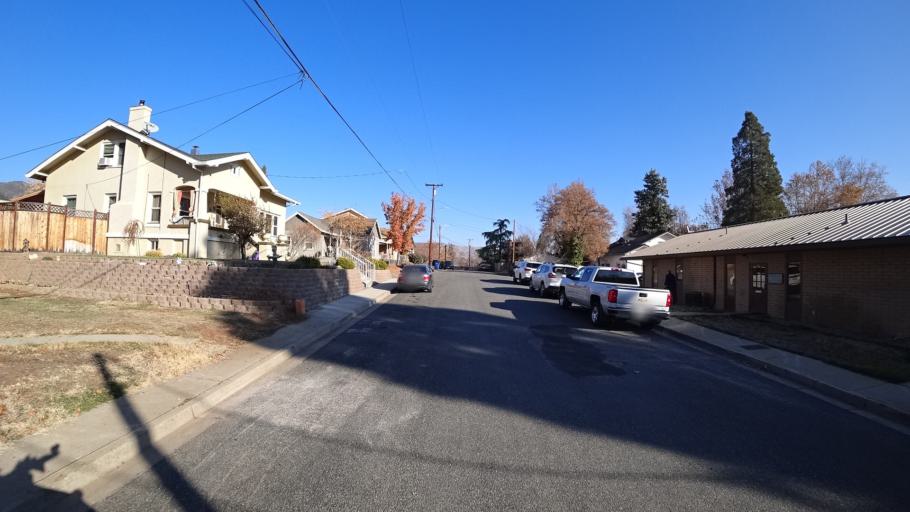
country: US
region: California
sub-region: Siskiyou County
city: Yreka
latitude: 41.7375
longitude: -122.6349
